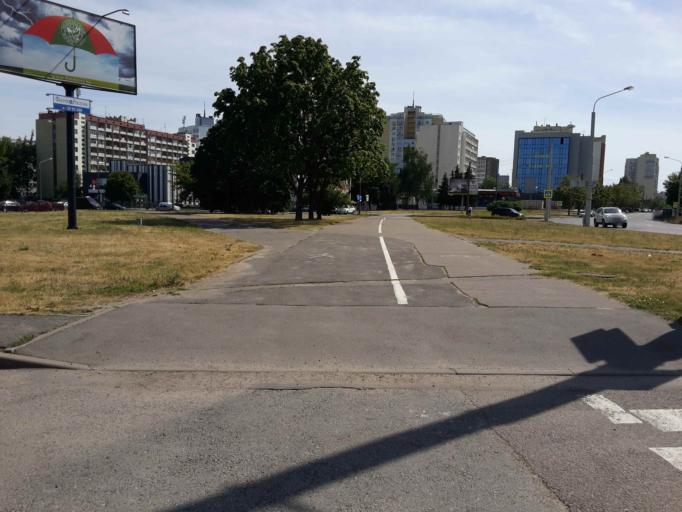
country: BY
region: Minsk
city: Minsk
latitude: 53.9289
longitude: 27.5660
